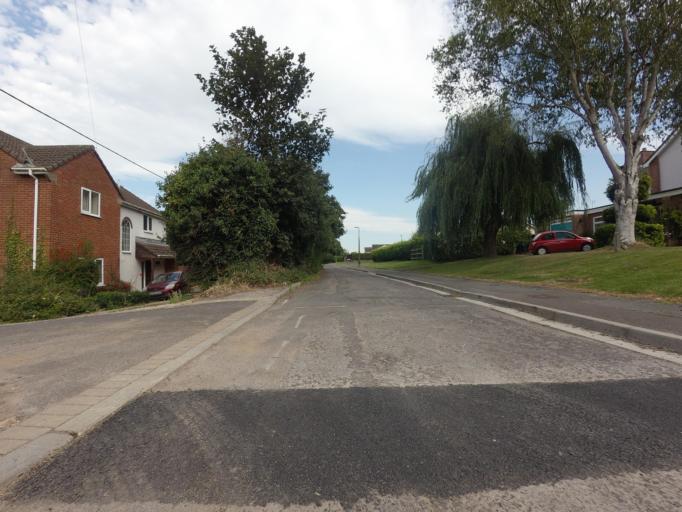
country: GB
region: England
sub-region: Wiltshire
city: Trowbridge
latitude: 51.3287
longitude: -2.1926
